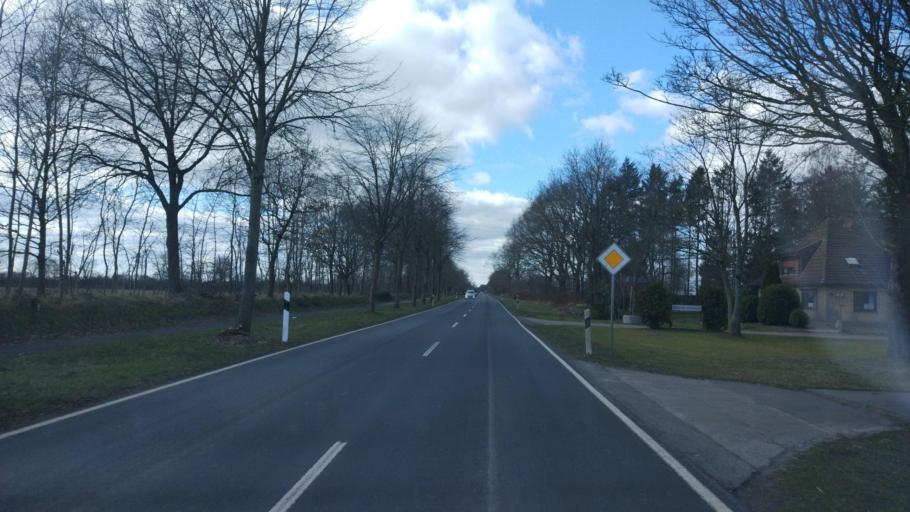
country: DE
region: Schleswig-Holstein
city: Gross Rheide
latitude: 54.4444
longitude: 9.4284
